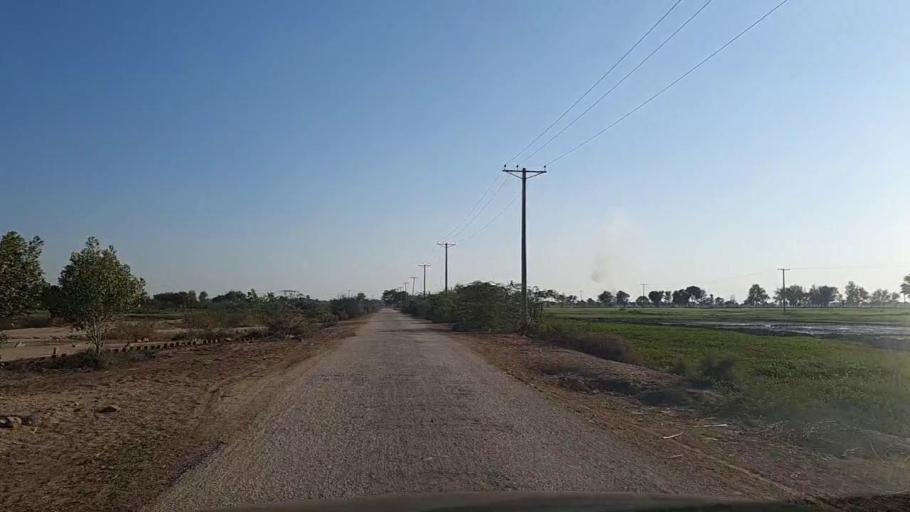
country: PK
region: Sindh
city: Nawabshah
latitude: 26.2120
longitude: 68.3735
